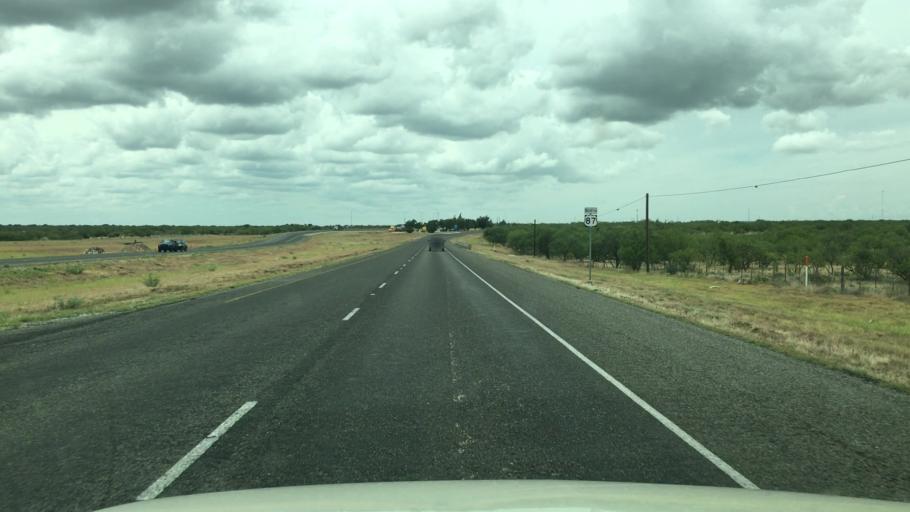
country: US
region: Texas
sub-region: Concho County
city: Eden
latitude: 31.2175
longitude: -99.9547
